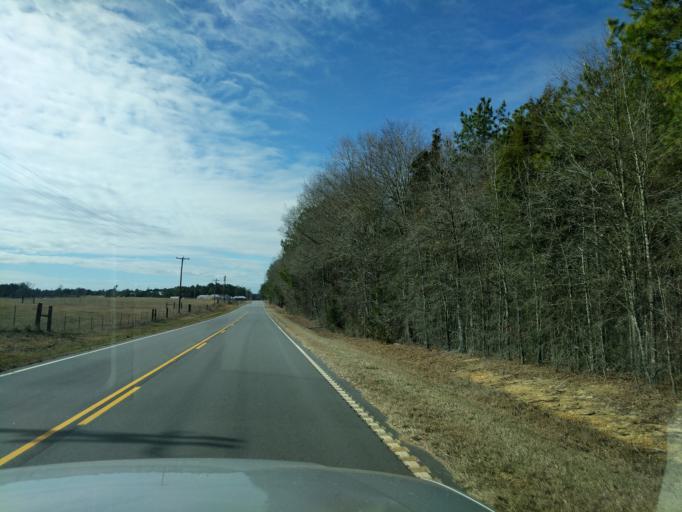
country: US
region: South Carolina
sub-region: Edgefield County
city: Edgefield
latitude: 33.9443
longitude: -81.9230
